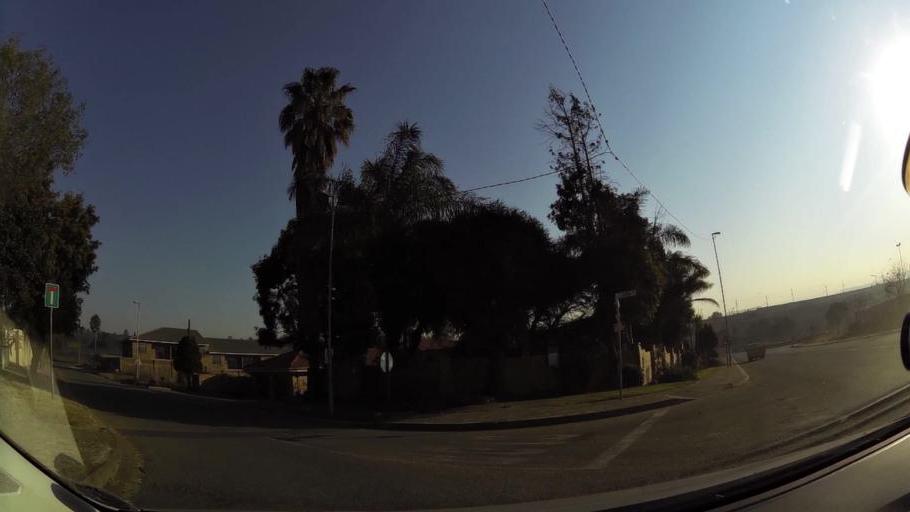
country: ZA
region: Gauteng
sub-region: City of Johannesburg Metropolitan Municipality
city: Modderfontein
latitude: -26.0869
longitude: 28.1036
